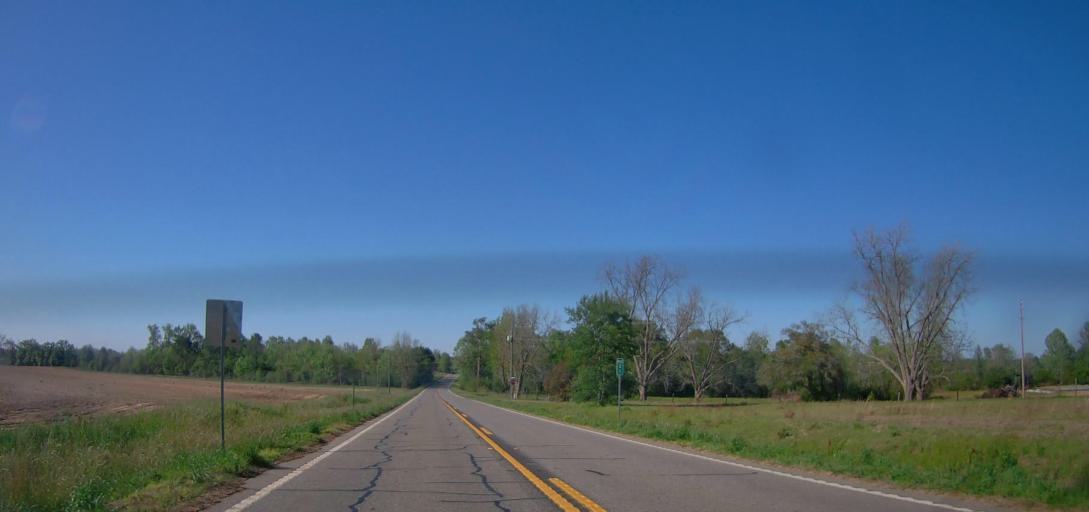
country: US
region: Georgia
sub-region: Wilcox County
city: Rochelle
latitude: 31.8121
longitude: -83.4890
